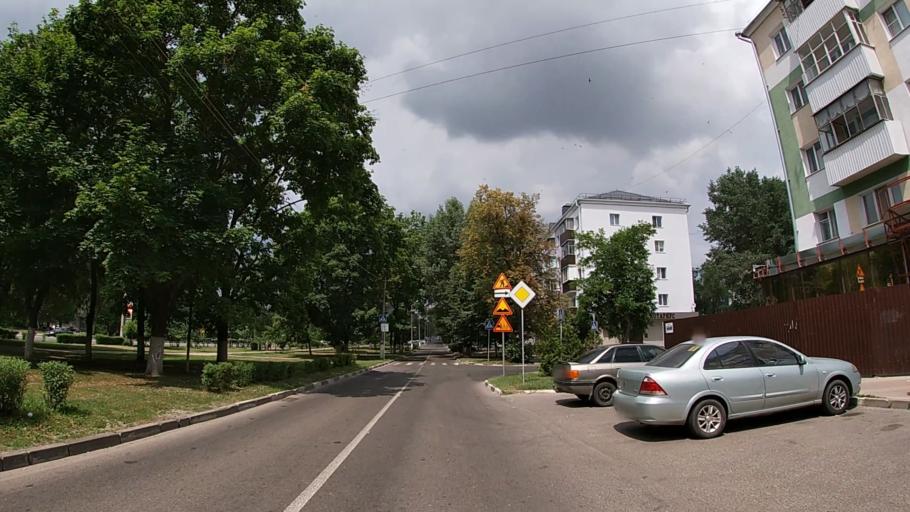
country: RU
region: Belgorod
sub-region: Belgorodskiy Rayon
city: Belgorod
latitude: 50.6142
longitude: 36.5788
